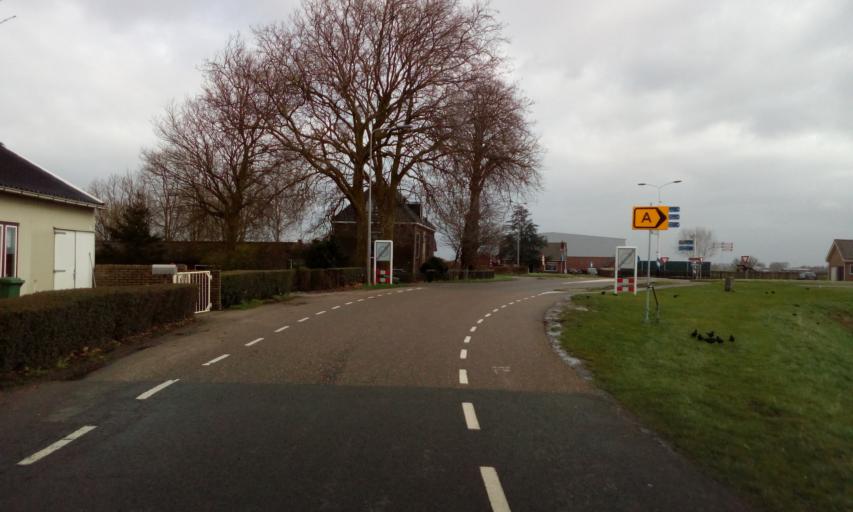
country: NL
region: North Holland
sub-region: Gemeente Aalsmeer
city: Aalsmeer
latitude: 52.2081
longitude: 4.7783
